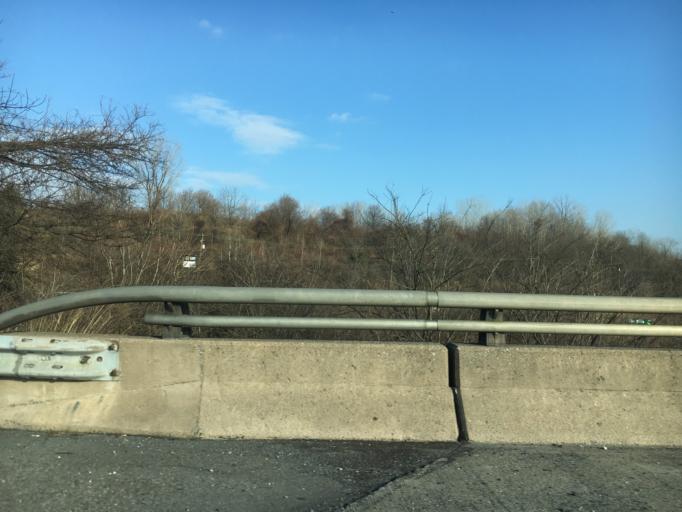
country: US
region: Pennsylvania
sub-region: Lehigh County
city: Stiles
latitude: 40.6718
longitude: -75.5158
